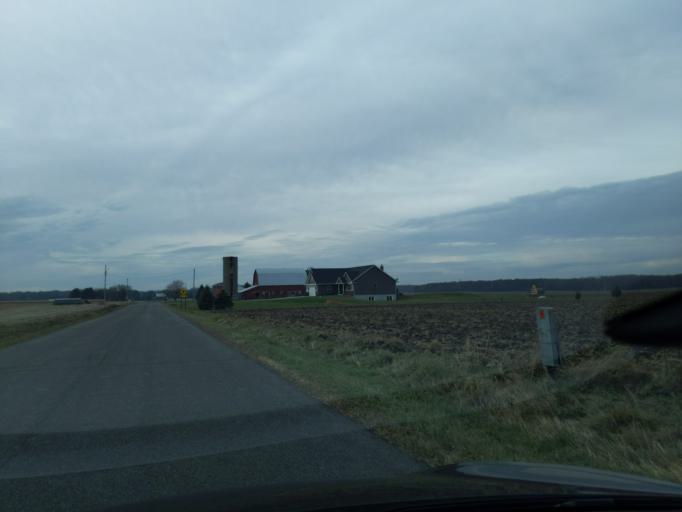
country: US
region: Michigan
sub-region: Ingham County
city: Okemos
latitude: 42.6546
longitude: -84.3800
